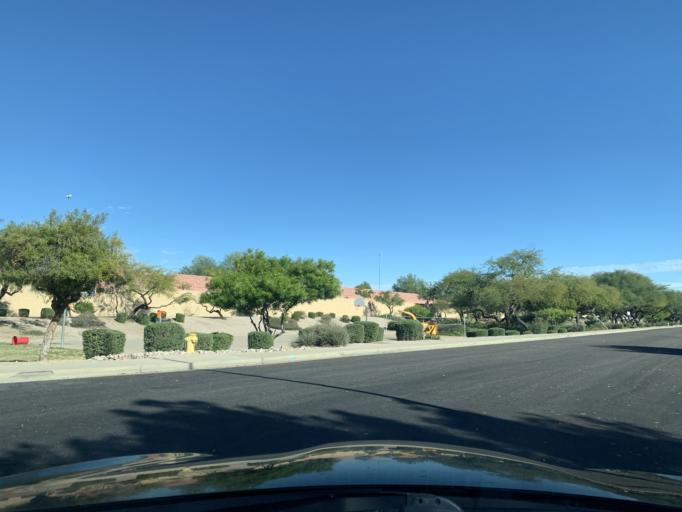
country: US
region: Arizona
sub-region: Pinal County
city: Apache Junction
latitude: 33.3856
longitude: -111.6279
